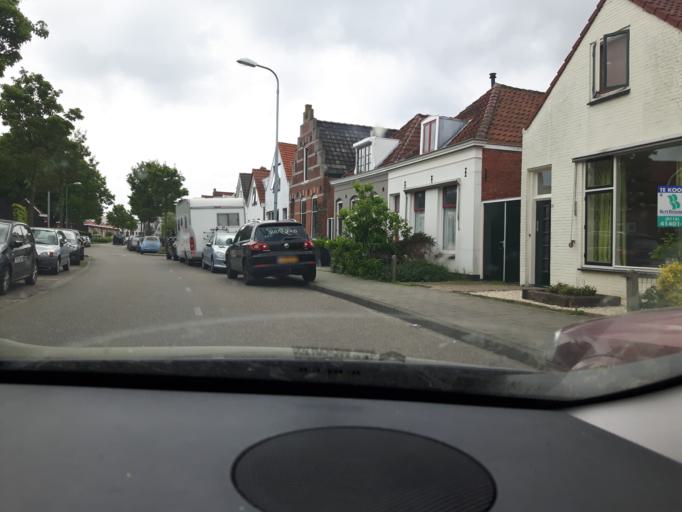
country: NL
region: Zeeland
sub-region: Gemeente Vlissingen
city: Vlissingen
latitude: 51.4623
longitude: 3.6025
